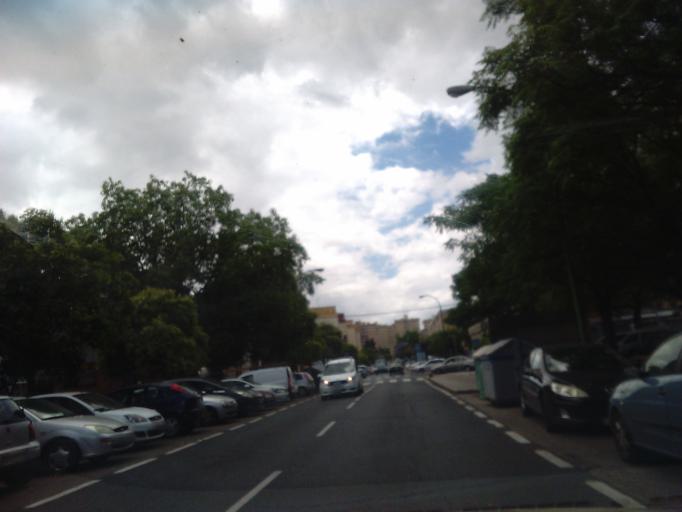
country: ES
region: Andalusia
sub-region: Provincia de Sevilla
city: Sevilla
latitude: 37.3779
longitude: -5.9520
